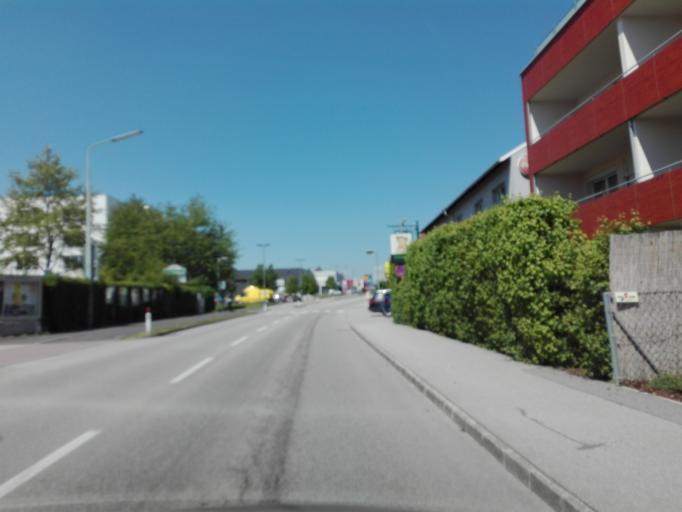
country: AT
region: Upper Austria
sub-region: Politischer Bezirk Linz-Land
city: Traun
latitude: 48.2379
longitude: 14.2628
